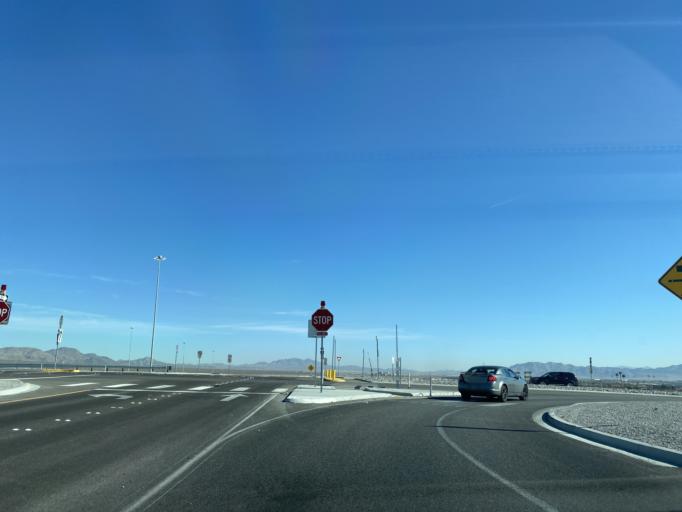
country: US
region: Nevada
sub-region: Clark County
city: North Las Vegas
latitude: 36.2924
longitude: -115.1538
